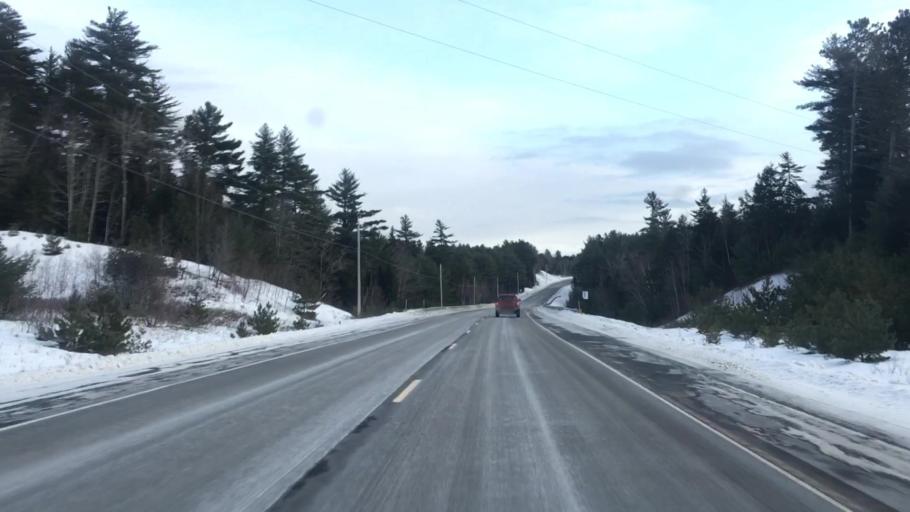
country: US
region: Maine
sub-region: Washington County
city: Addison
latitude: 44.9358
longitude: -67.7373
